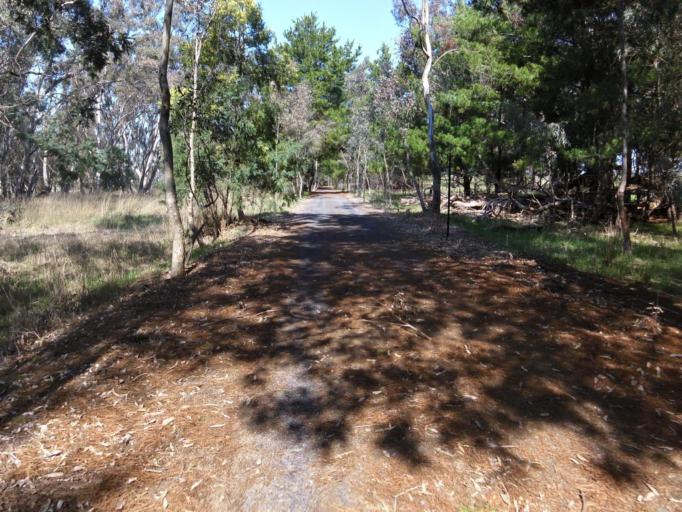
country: AU
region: Victoria
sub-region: Murrindindi
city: Alexandra
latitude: -36.9966
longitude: 145.7421
